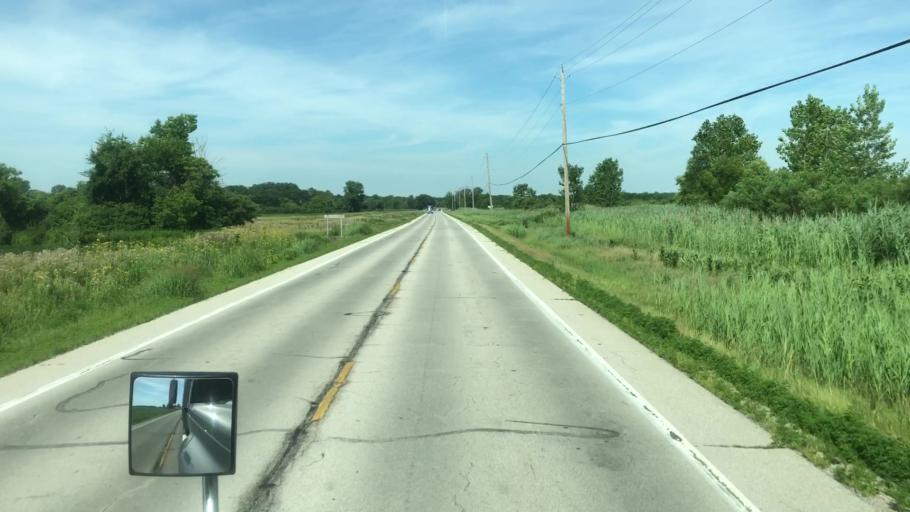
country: US
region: Ohio
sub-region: Ottawa County
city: Port Clinton
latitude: 41.4086
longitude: -82.9382
